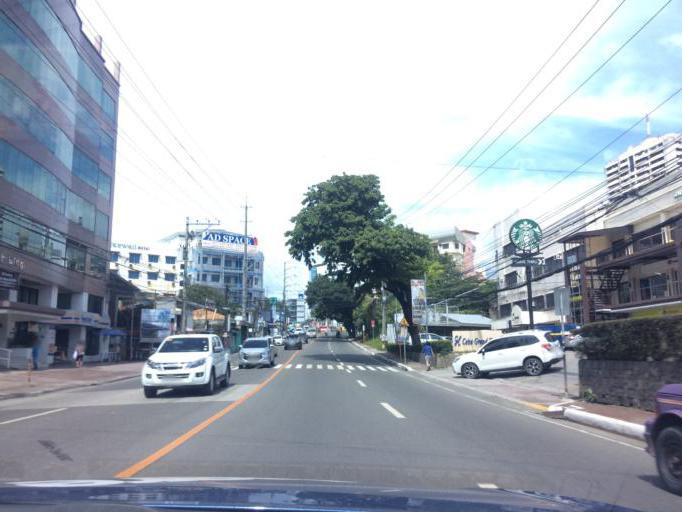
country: PH
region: Central Visayas
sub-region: Province of Cebu
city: Cebu City
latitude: 10.3179
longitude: 123.8962
